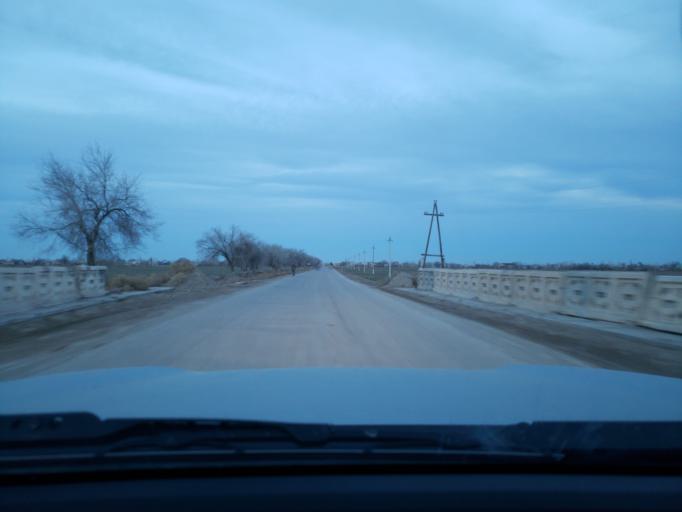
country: TM
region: Dasoguz
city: Tagta
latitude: 41.6255
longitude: 60.0621
